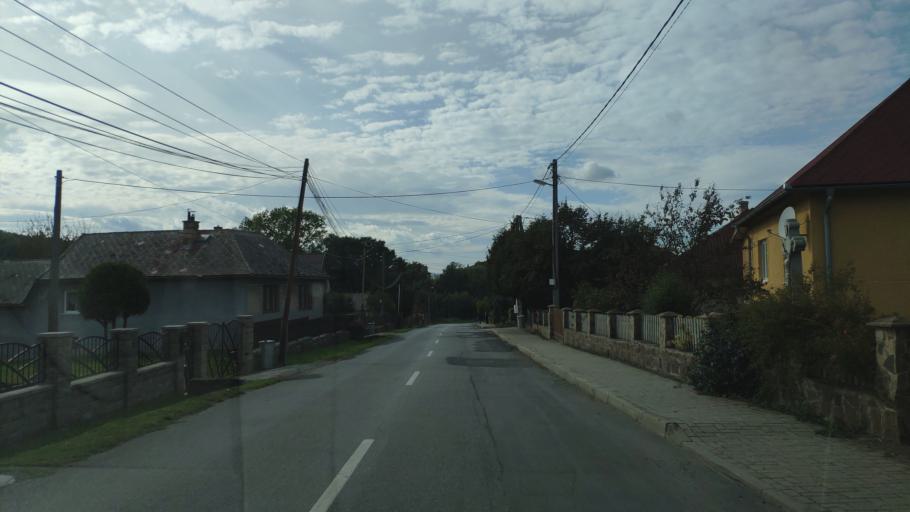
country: SK
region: Presovsky
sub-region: Okres Presov
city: Presov
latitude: 48.9515
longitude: 21.3114
